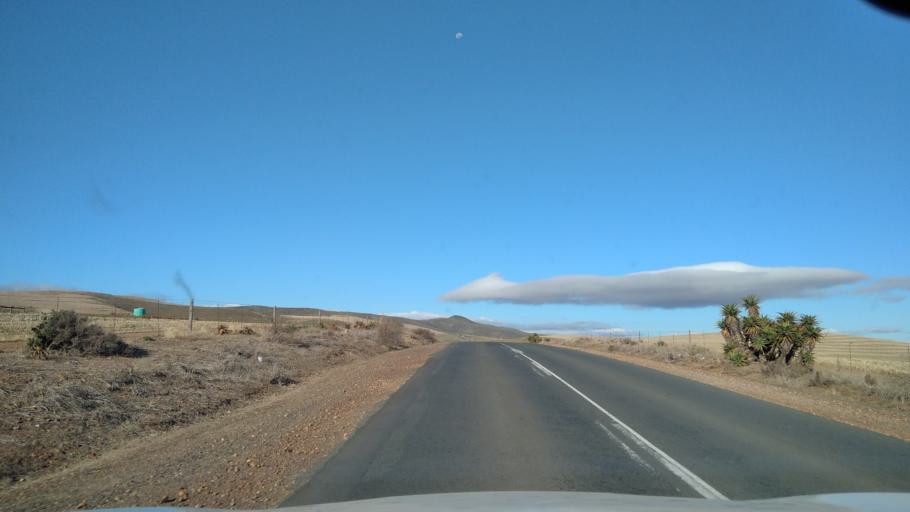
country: ZA
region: Western Cape
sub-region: Overberg District Municipality
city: Caledon
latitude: -34.1694
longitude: 19.2890
